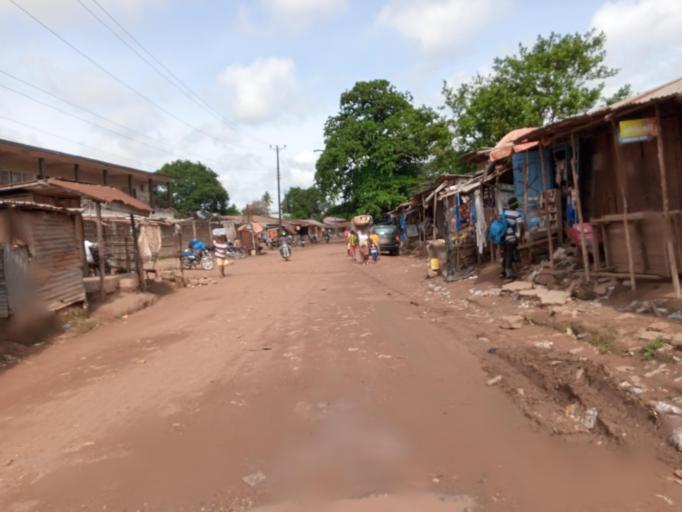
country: SL
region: Southern Province
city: Bo
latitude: 7.9600
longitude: -11.7438
